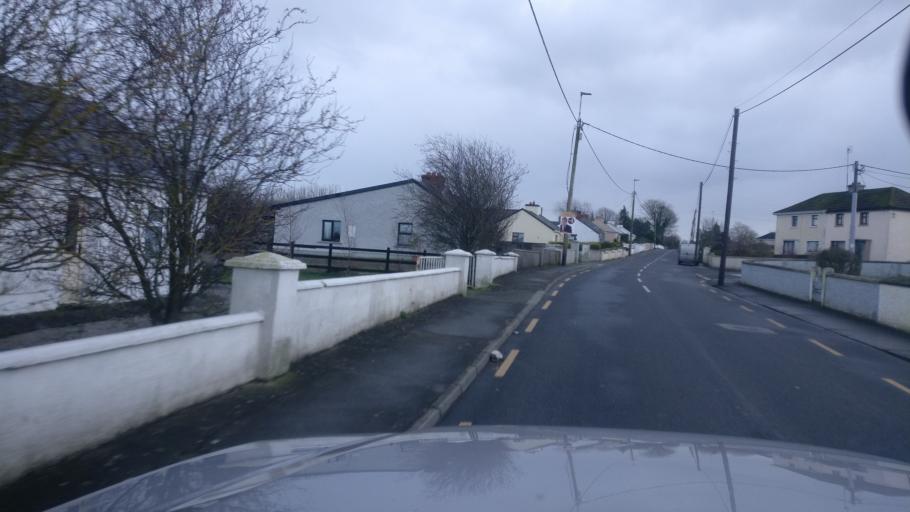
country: IE
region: Munster
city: Nenagh Bridge
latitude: 52.9929
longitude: -8.1228
